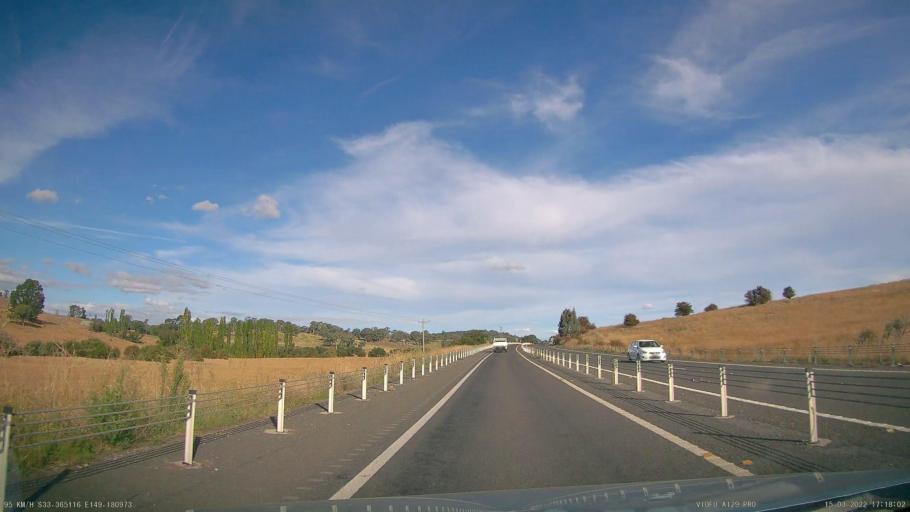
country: AU
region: New South Wales
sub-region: Blayney
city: Millthorpe
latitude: -33.3654
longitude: 149.1811
